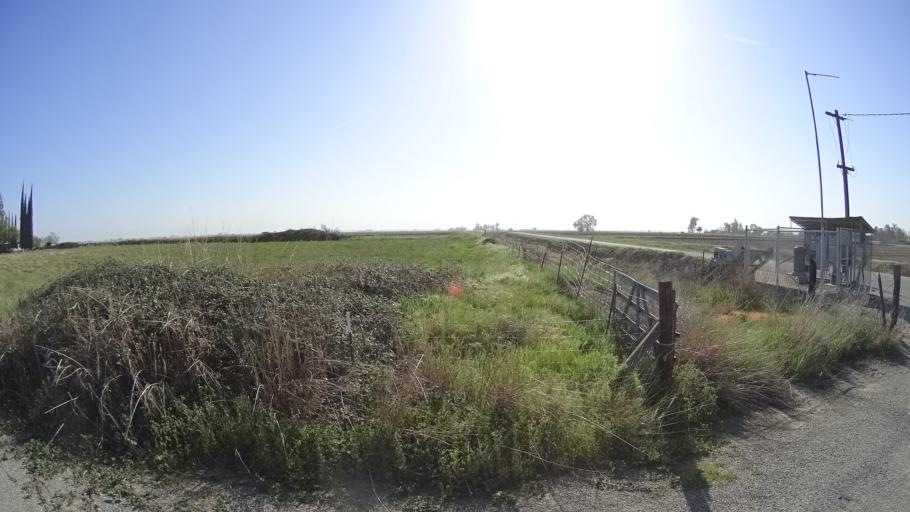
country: US
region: California
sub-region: Glenn County
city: Willows
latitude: 39.5589
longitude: -122.1081
